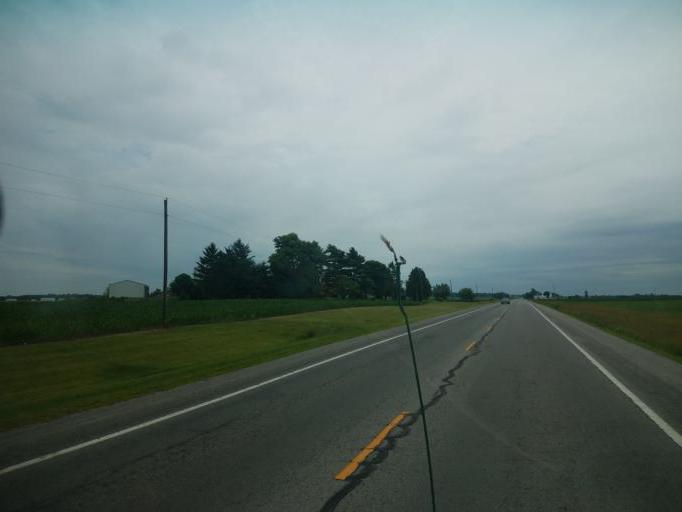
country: US
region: Ohio
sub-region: Hardin County
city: Kenton
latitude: 40.6774
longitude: -83.6719
